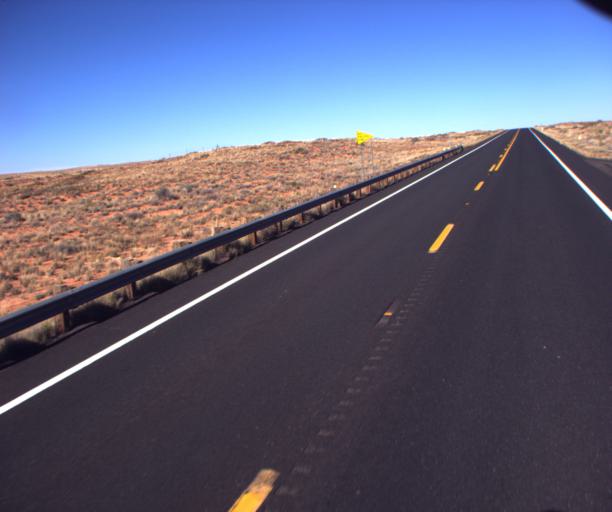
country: US
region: Arizona
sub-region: Coconino County
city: Kaibito
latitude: 36.3548
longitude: -110.9070
